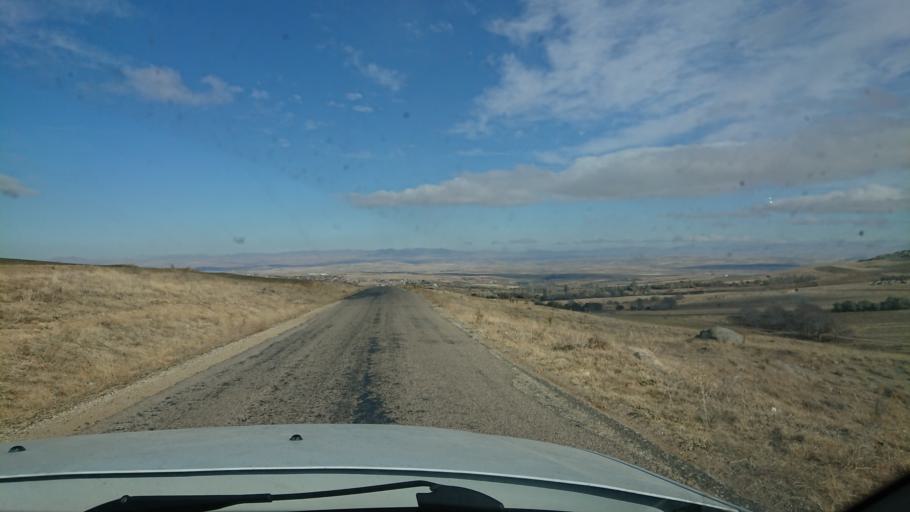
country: TR
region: Aksaray
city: Agacoren
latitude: 38.8413
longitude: 33.9527
